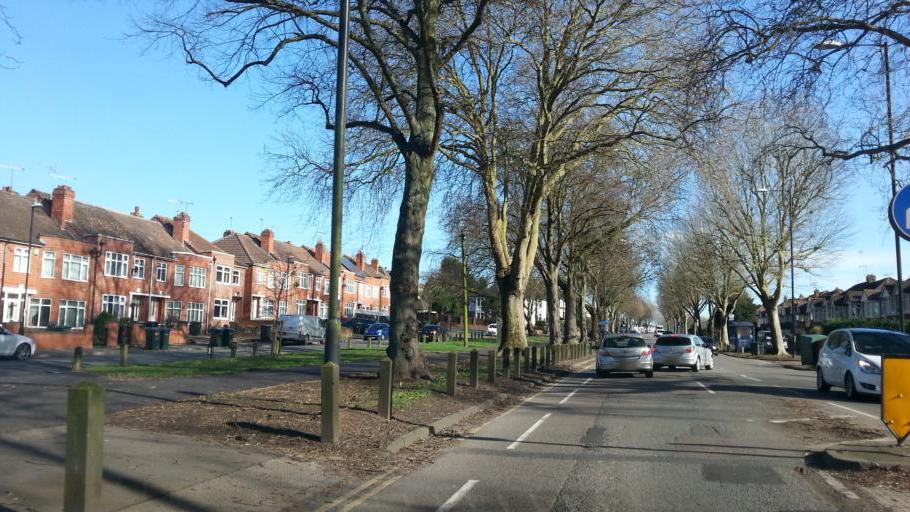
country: GB
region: England
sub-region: Coventry
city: Coventry
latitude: 52.4177
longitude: -1.5436
